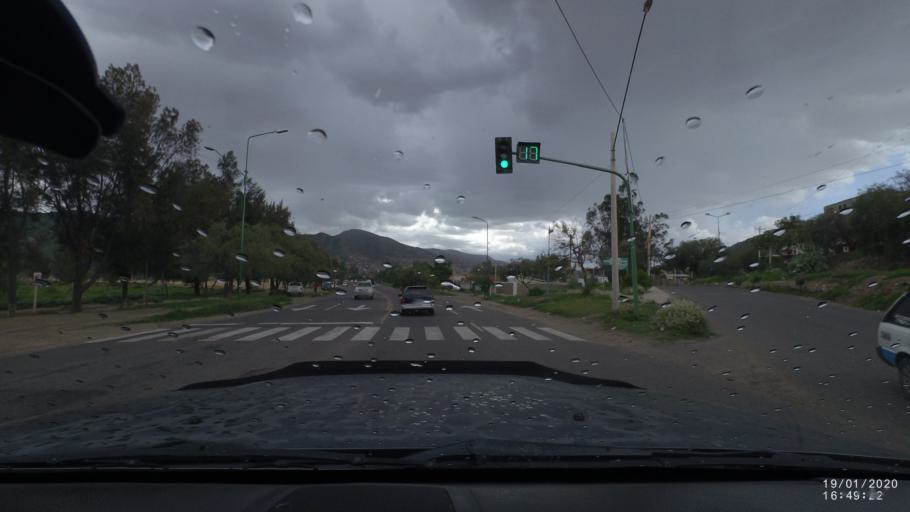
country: BO
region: Cochabamba
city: Cochabamba
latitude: -17.4160
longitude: -66.1410
